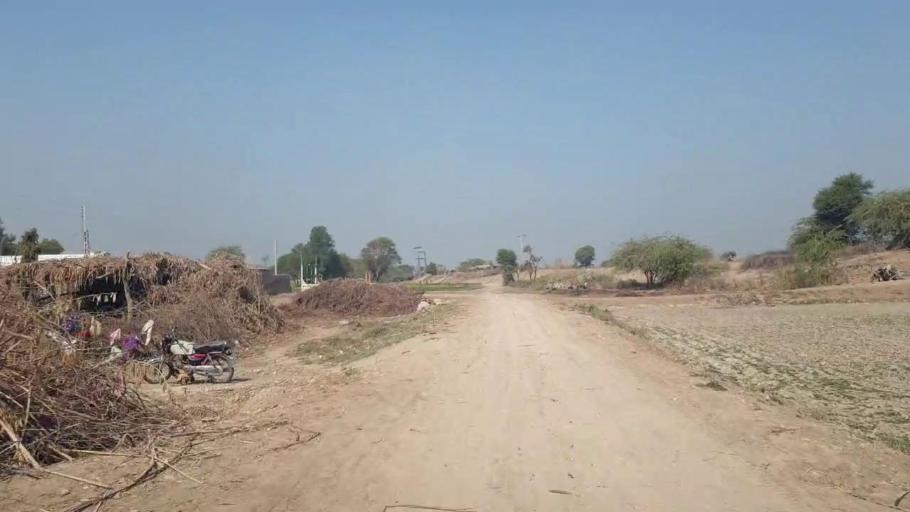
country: PK
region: Sindh
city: Chambar
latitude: 25.3530
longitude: 68.8469
